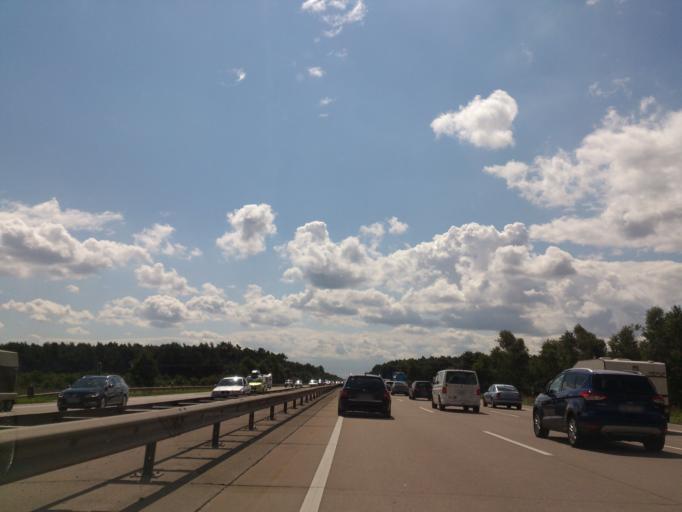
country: DE
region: Lower Saxony
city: Lindwedel
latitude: 52.6409
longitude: 9.7134
